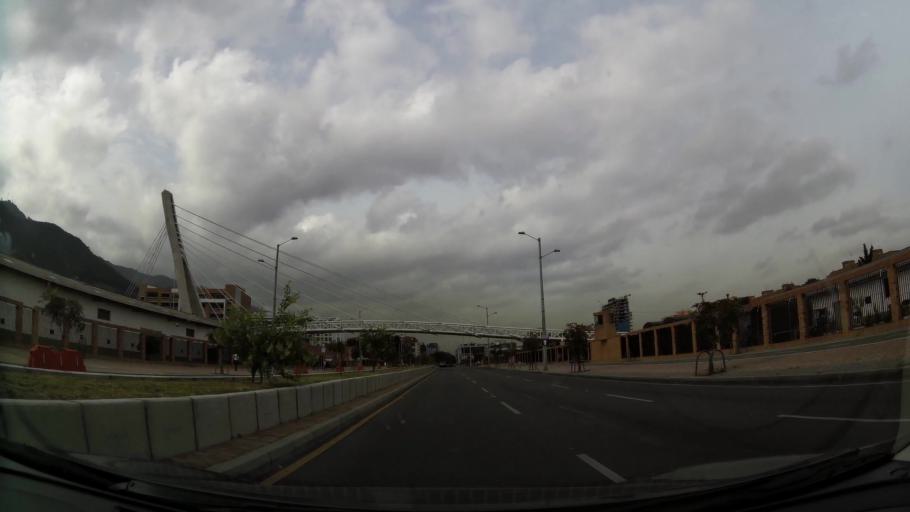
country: CO
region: Bogota D.C.
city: Barrio San Luis
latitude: 4.6858
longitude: -74.0418
